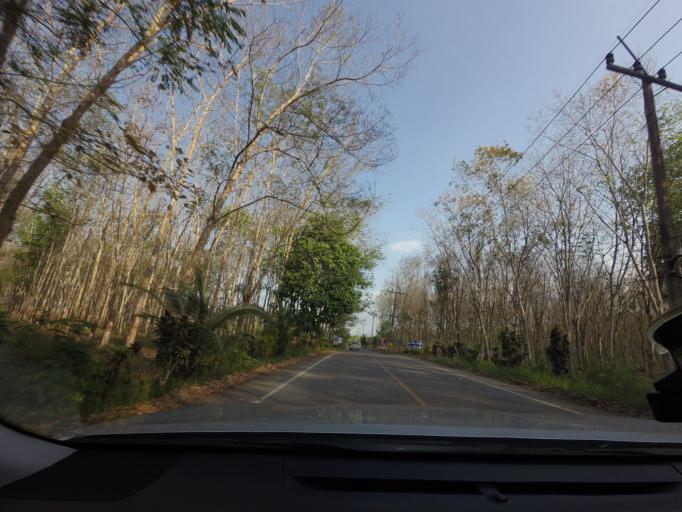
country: TH
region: Surat Thani
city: Phrasaeng
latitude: 8.5535
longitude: 99.2997
